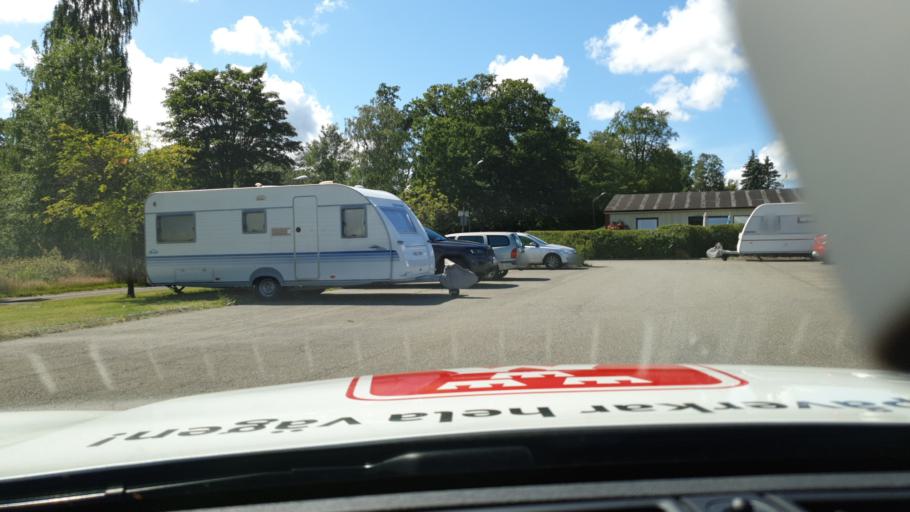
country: SE
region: Skane
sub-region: Hassleholms Kommun
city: Hassleholm
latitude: 56.1537
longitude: 13.7470
